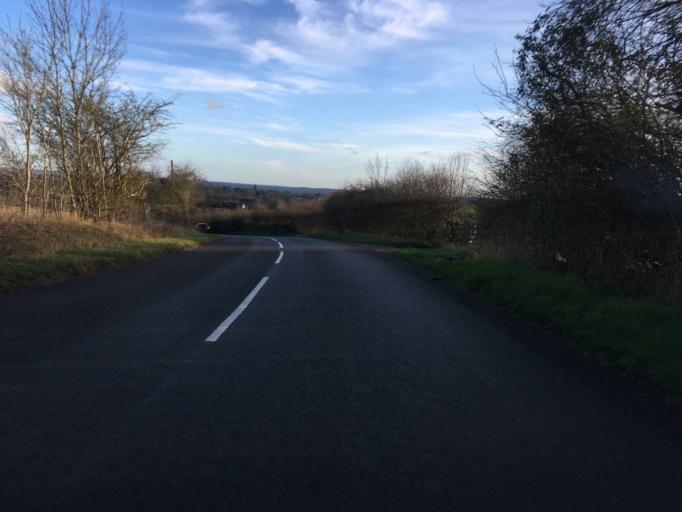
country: GB
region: England
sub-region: Warwickshire
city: Stratford-upon-Avon
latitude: 52.2125
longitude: -1.6848
